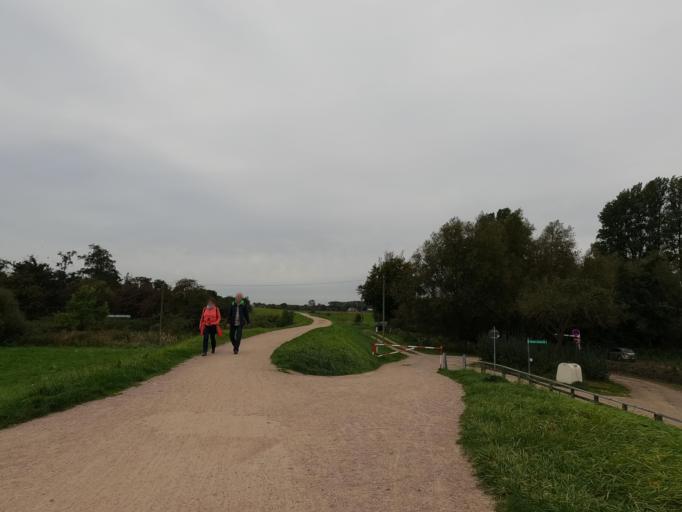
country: DE
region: Schleswig-Holstein
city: Kellenhusen
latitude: 54.1728
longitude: 11.0294
